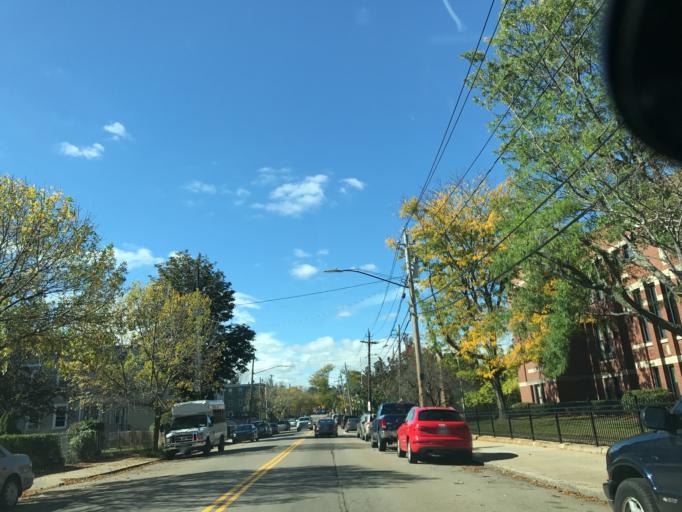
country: US
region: Massachusetts
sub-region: Suffolk County
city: South Boston
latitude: 42.2982
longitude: -71.0576
